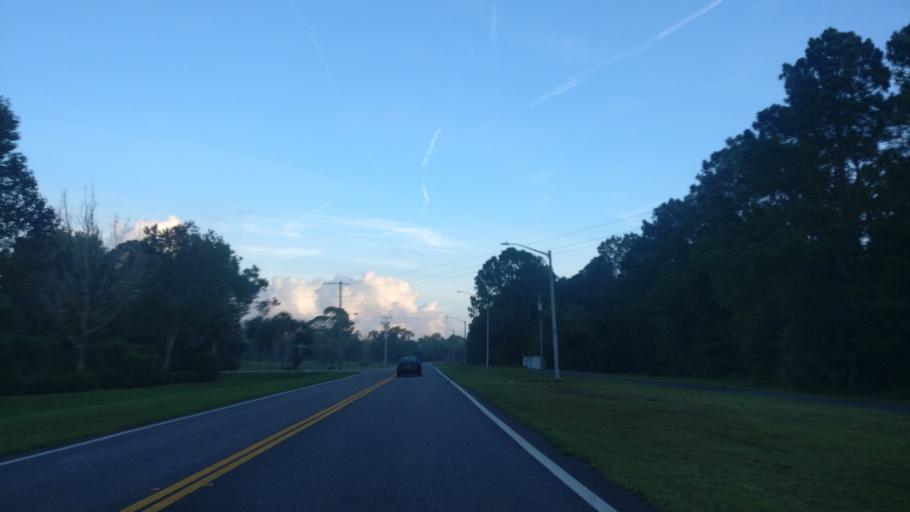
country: US
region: Florida
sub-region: Flagler County
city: Palm Coast
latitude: 29.5319
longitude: -81.2384
